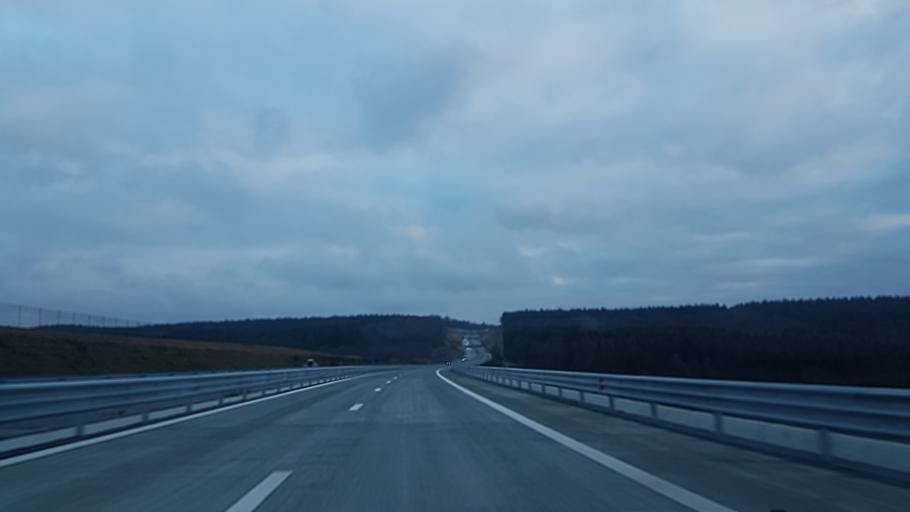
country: BE
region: Wallonia
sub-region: Province de Namur
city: Couvin
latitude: 50.0124
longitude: 4.5349
